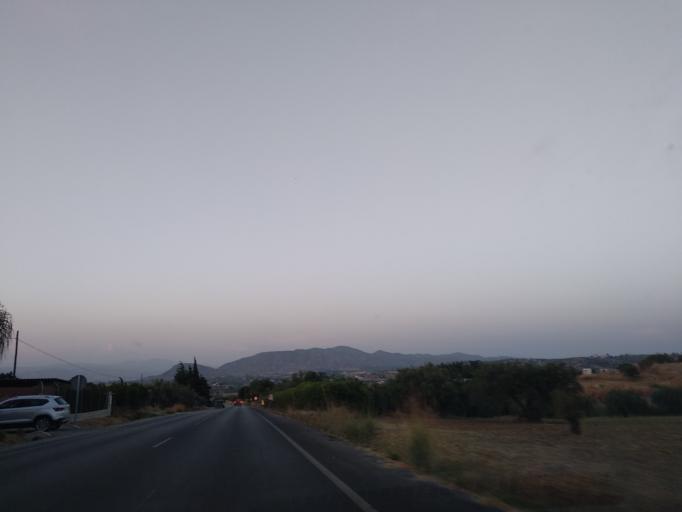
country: ES
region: Andalusia
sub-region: Provincia de Malaga
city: Alhaurin el Grande
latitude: 36.6590
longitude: -4.6734
